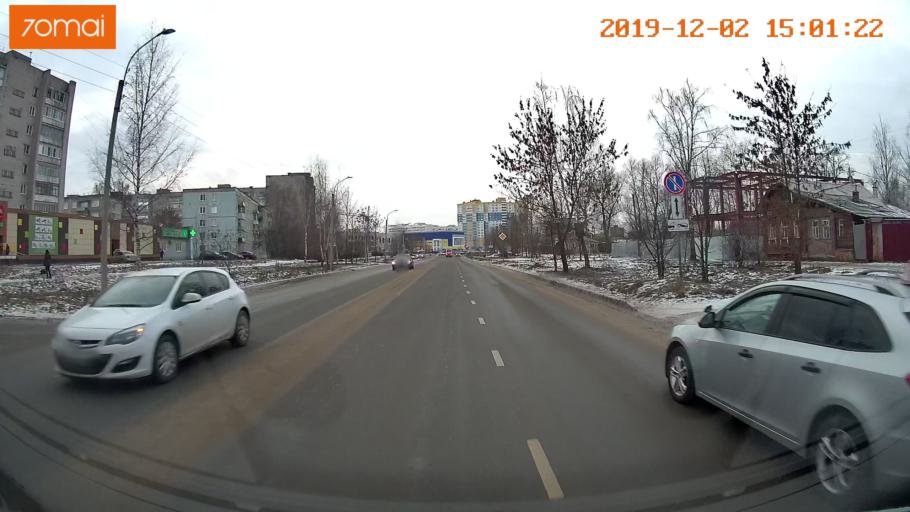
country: RU
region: Ivanovo
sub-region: Gorod Ivanovo
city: Ivanovo
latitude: 56.9724
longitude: 40.9969
